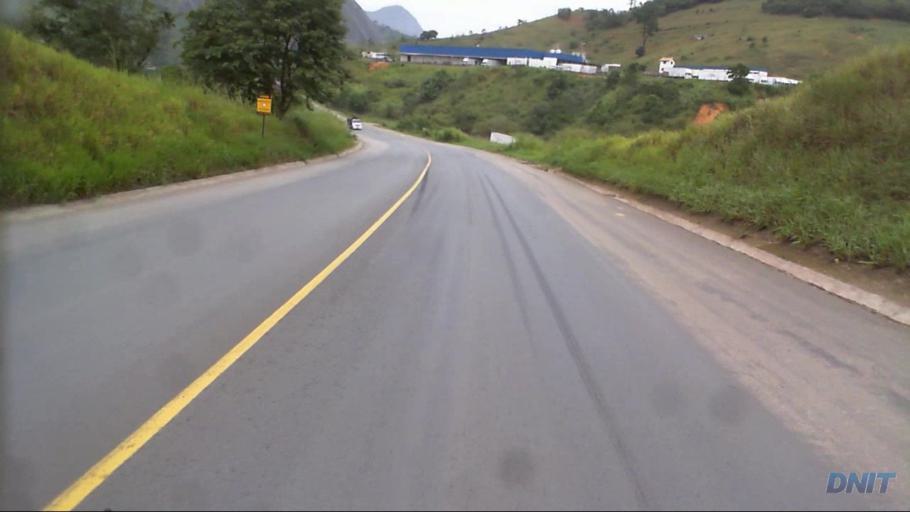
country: BR
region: Minas Gerais
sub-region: Coronel Fabriciano
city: Coronel Fabriciano
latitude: -19.5292
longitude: -42.6716
